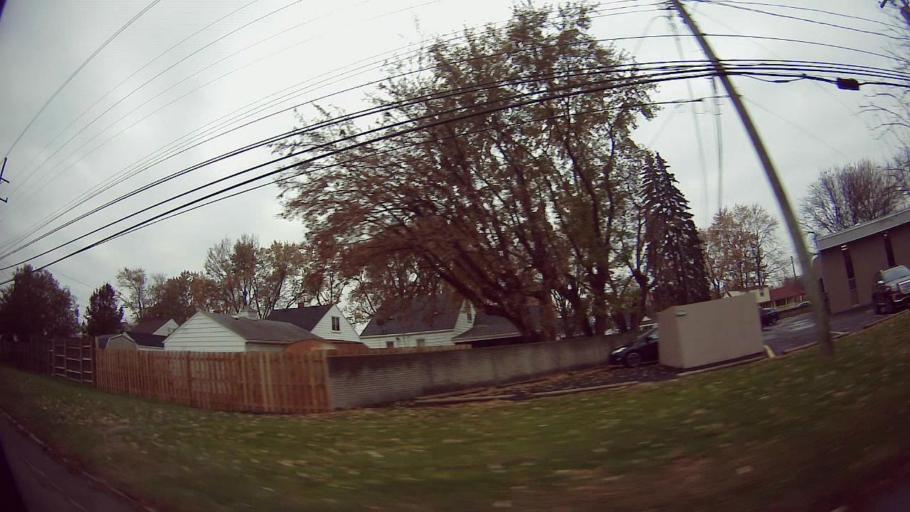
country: US
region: Michigan
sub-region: Wayne County
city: Dearborn Heights
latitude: 42.3525
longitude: -83.2744
